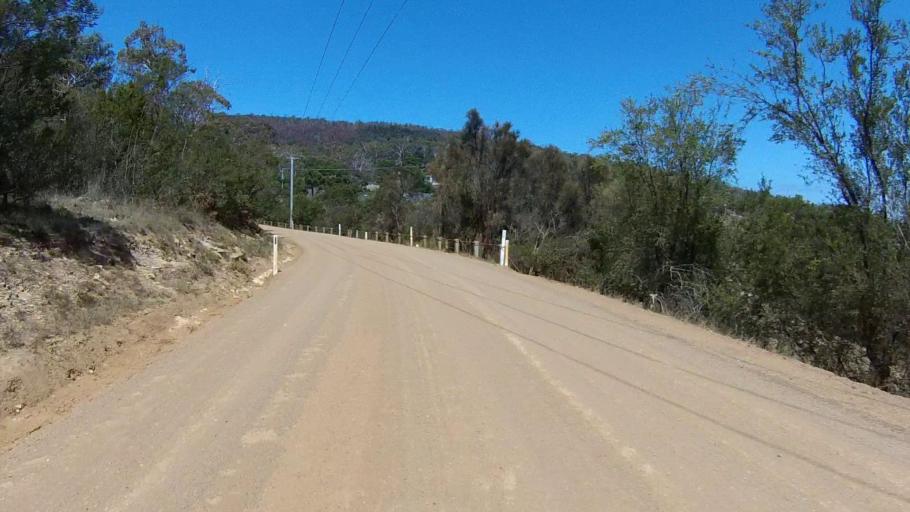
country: AU
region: Tasmania
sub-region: Clarence
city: Lauderdale
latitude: -42.9309
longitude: 147.4659
